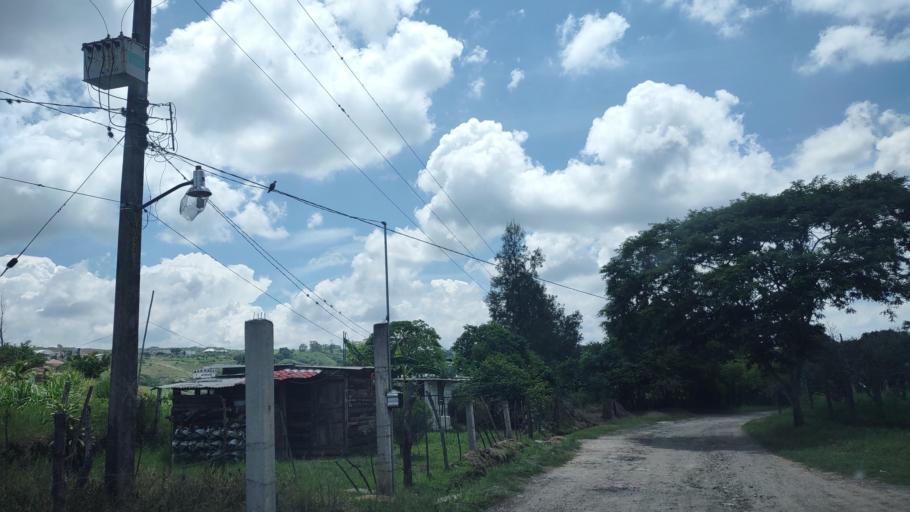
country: MX
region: Veracruz
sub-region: Emiliano Zapata
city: Dos Rios
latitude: 19.4946
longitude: -96.8109
